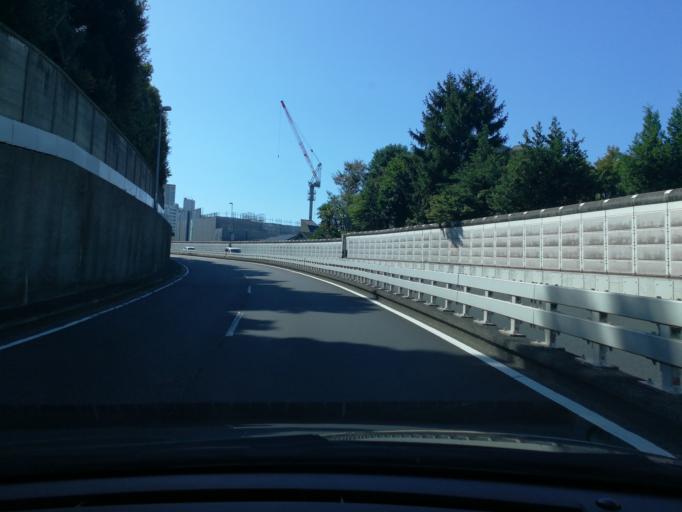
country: JP
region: Tokyo
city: Tokyo
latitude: 35.6404
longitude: 139.7174
